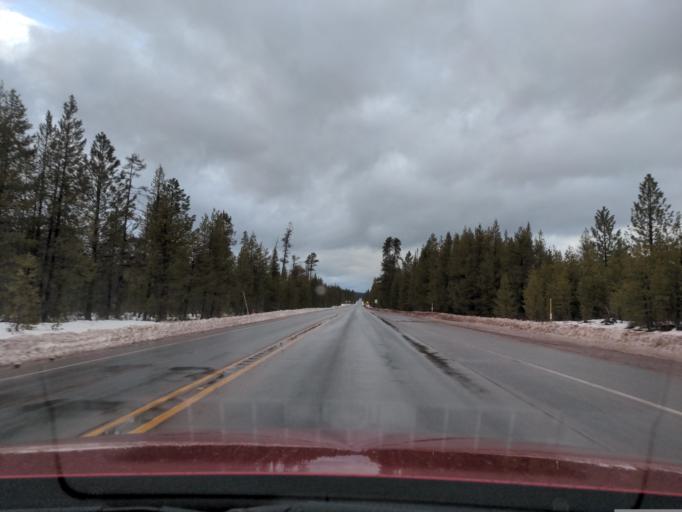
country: US
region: Oregon
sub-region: Deschutes County
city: La Pine
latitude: 43.3339
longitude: -121.7595
